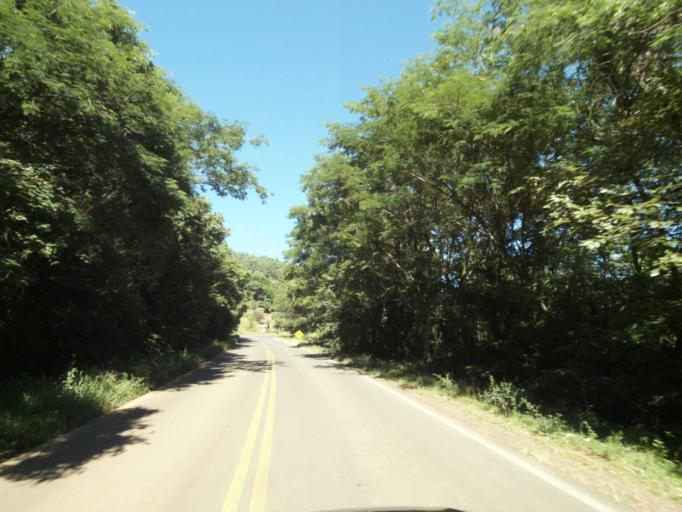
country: BR
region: Parana
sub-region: Francisco Beltrao
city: Francisco Beltrao
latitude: -26.1457
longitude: -53.3179
